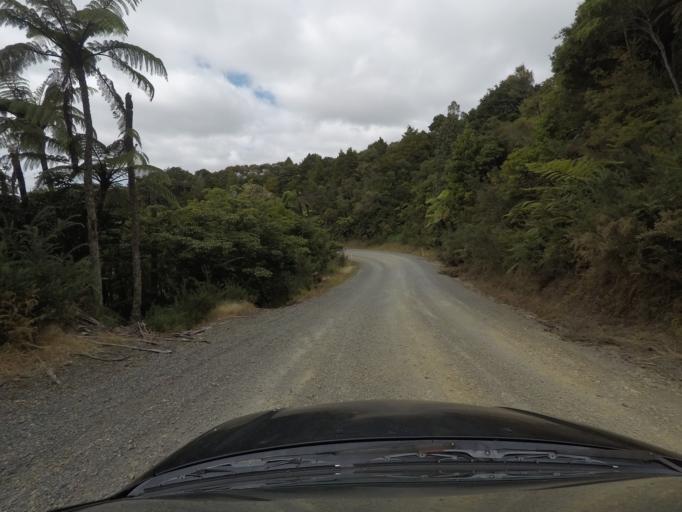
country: NZ
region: Northland
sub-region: Whangarei
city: Ruakaka
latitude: -35.9261
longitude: 174.3383
